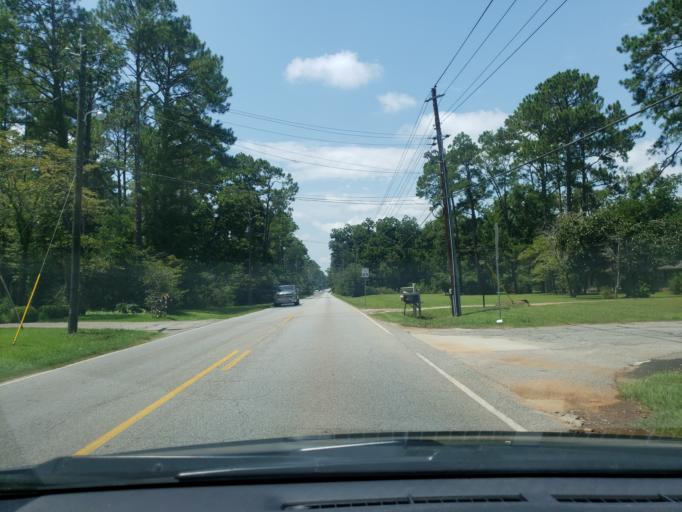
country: US
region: Georgia
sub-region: Dougherty County
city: Albany
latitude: 31.6135
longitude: -84.2283
